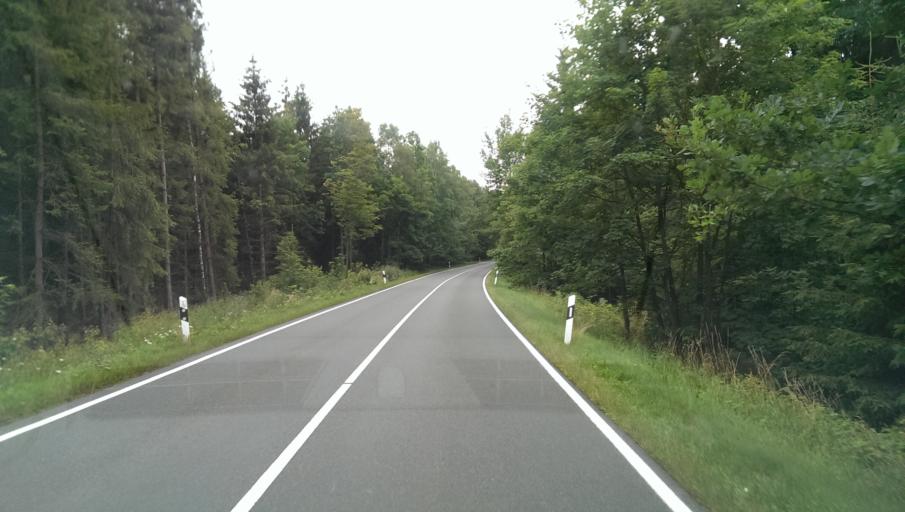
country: DE
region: Saxony
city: Pausa
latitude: 50.6059
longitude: 11.9971
